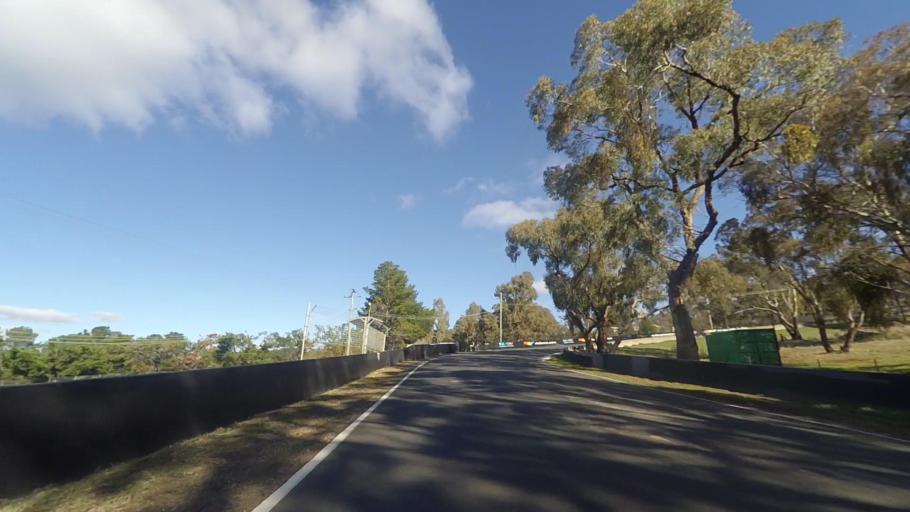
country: AU
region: New South Wales
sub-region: Bathurst Regional
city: Perthville
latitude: -33.4483
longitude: 149.5538
